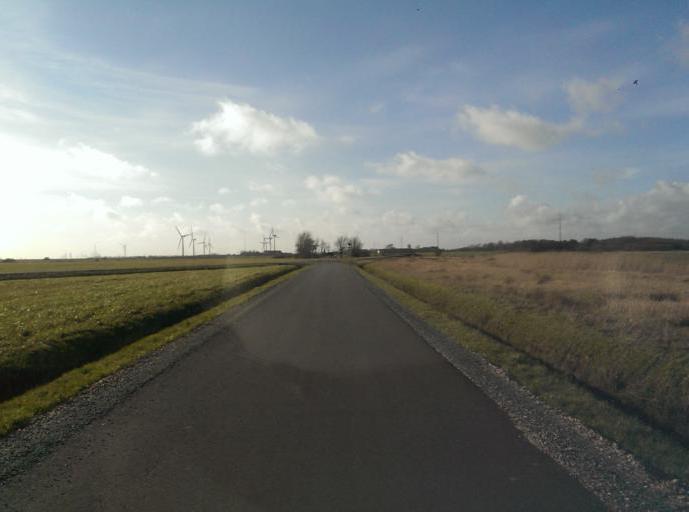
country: DK
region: South Denmark
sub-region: Esbjerg Kommune
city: Tjaereborg
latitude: 55.4406
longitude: 8.6263
